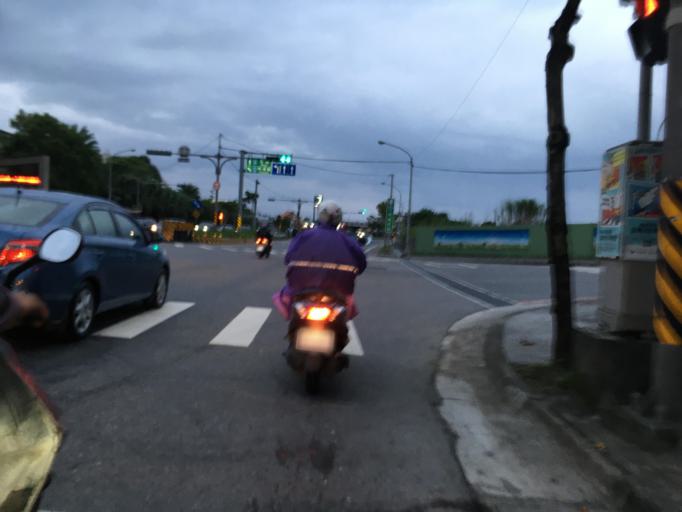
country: TW
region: Taiwan
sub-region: Yilan
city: Yilan
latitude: 24.6338
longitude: 121.8319
